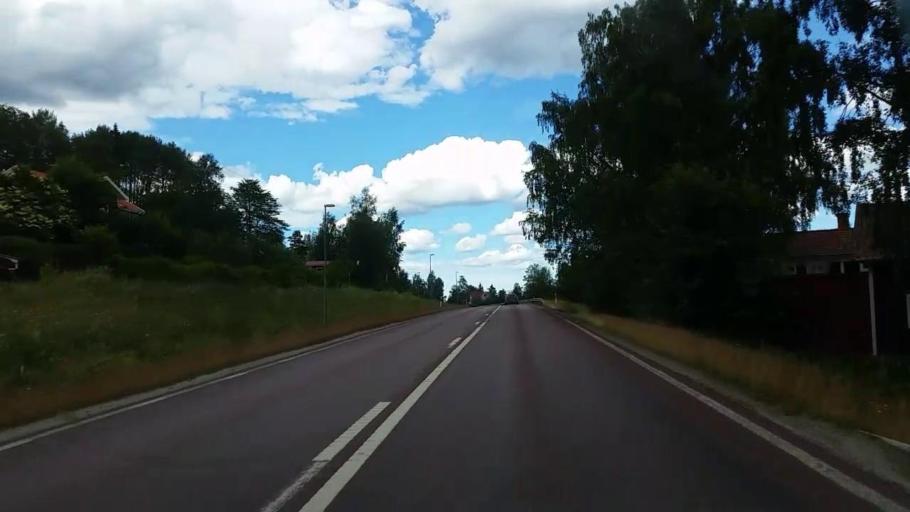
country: SE
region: Gaevleborg
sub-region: Ljusdals Kommun
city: Jaervsoe
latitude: 61.6998
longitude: 16.1635
